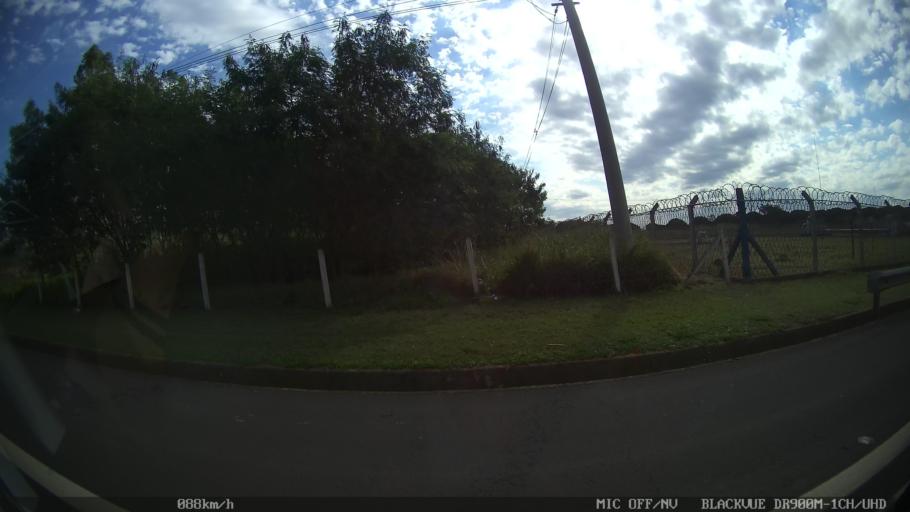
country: BR
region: Sao Paulo
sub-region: Iracemapolis
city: Iracemapolis
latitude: -22.6051
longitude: -47.4749
